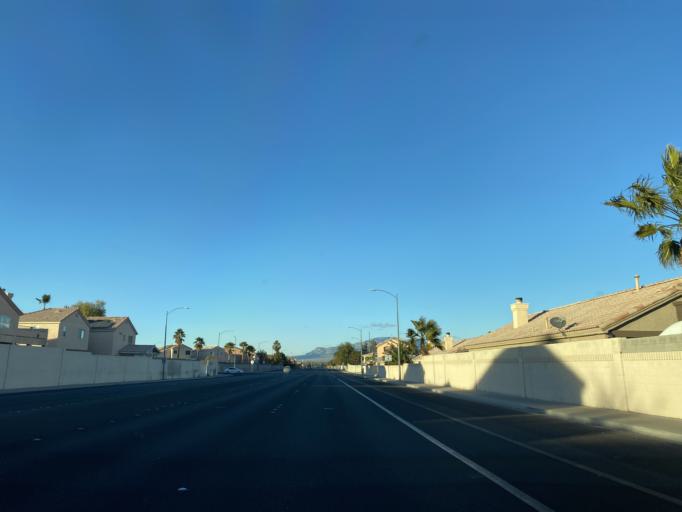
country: US
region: Nevada
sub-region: Clark County
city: Summerlin South
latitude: 36.2248
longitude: -115.2973
